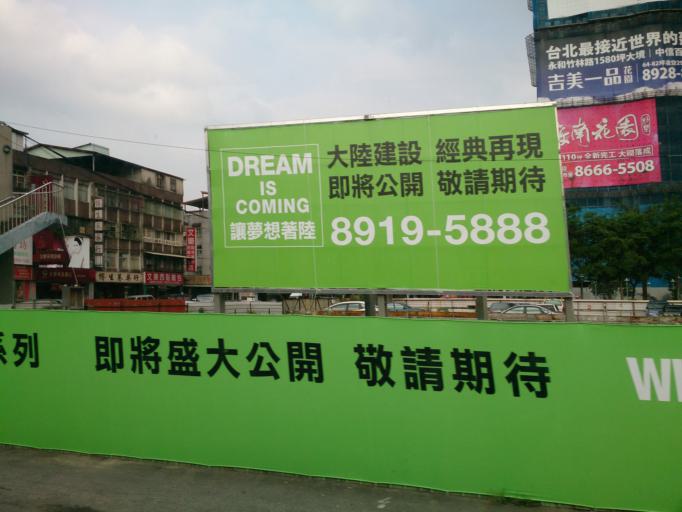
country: TW
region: Taipei
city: Taipei
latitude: 24.9702
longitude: 121.5425
